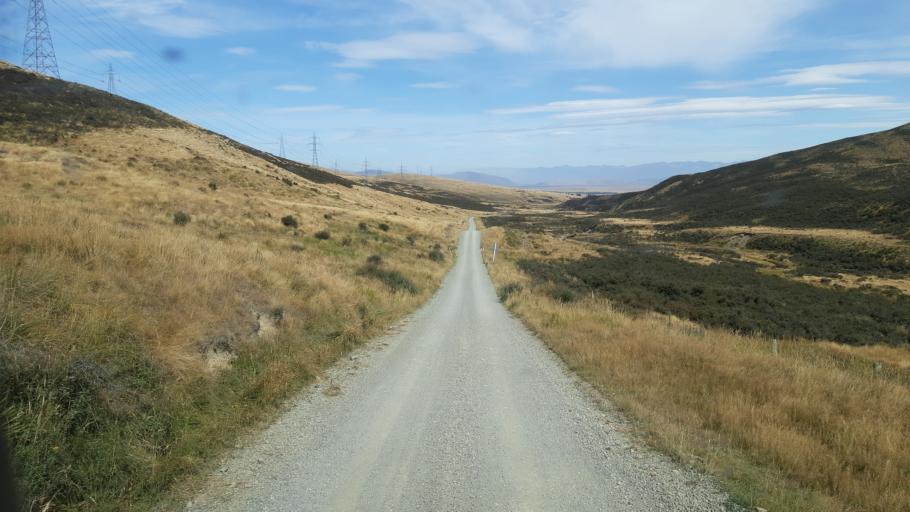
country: NZ
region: Canterbury
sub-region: Timaru District
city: Pleasant Point
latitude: -44.1932
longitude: 170.6040
